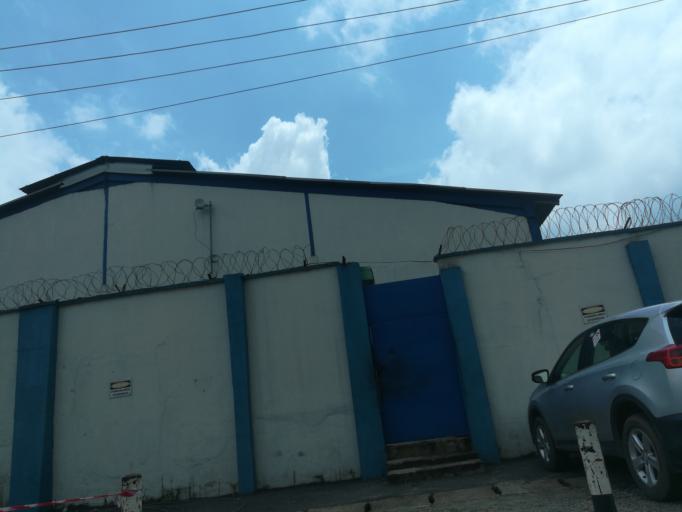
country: NG
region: Lagos
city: Somolu
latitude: 6.5538
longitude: 3.3586
